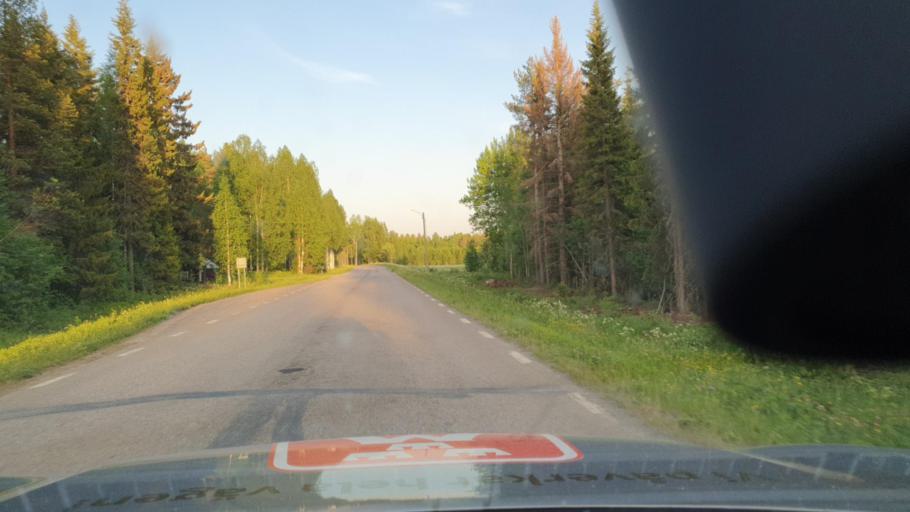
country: SE
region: Norrbotten
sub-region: Bodens Kommun
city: Boden
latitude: 66.0466
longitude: 21.7886
